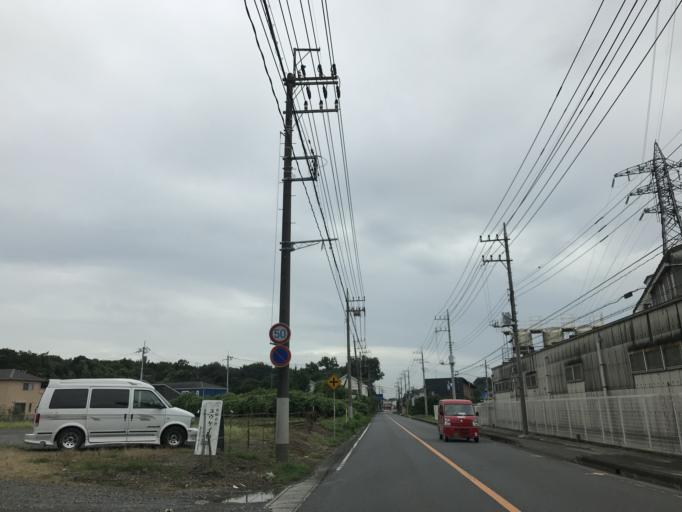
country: JP
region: Ibaraki
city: Koga
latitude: 36.1717
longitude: 139.7662
